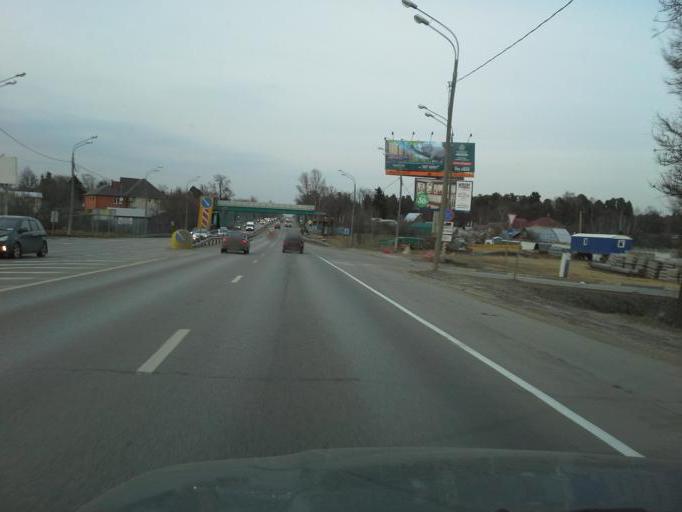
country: RU
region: Moscow
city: Novo-Peredelkino
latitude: 55.6711
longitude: 37.3129
